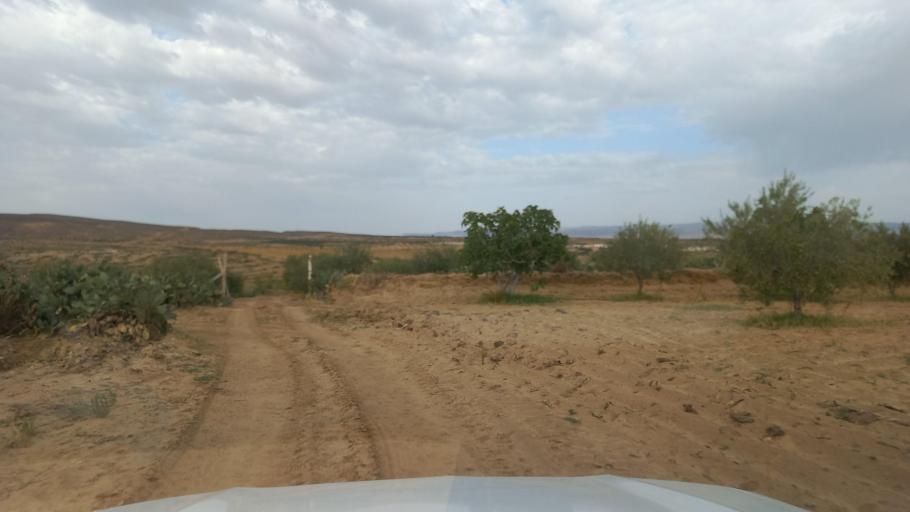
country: TN
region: Al Qasrayn
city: Kasserine
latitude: 35.1945
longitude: 9.0458
